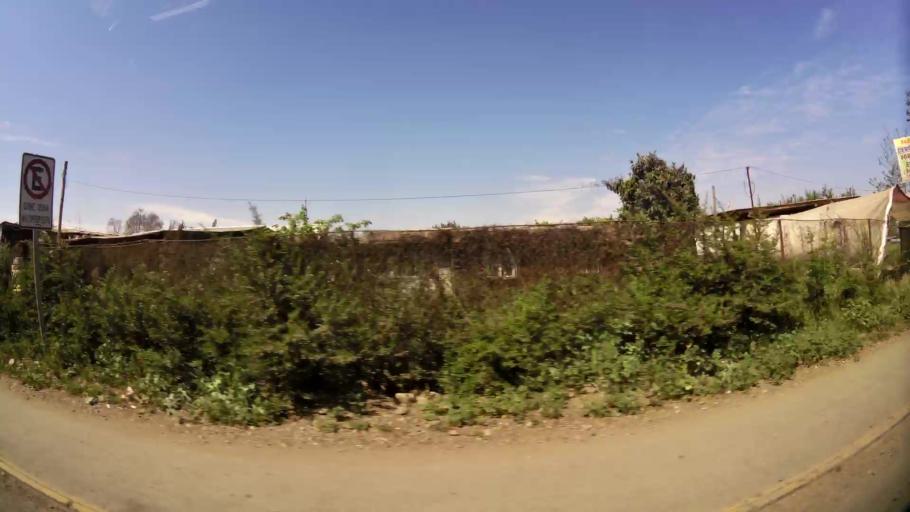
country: CL
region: Santiago Metropolitan
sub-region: Provincia de Talagante
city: Talagante
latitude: -33.6478
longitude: -70.9183
